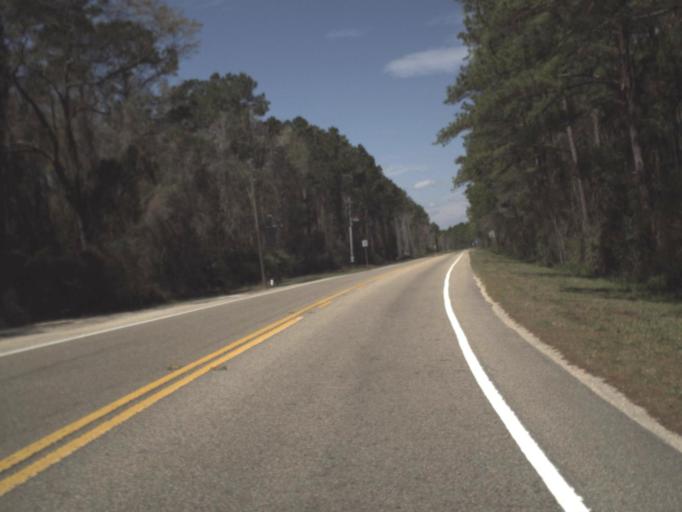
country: US
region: Florida
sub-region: Leon County
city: Woodville
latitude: 30.2007
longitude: -84.1847
